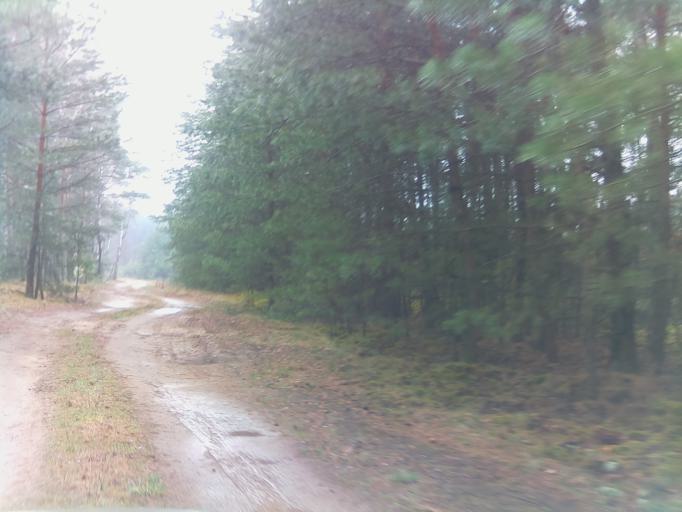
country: DE
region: Brandenburg
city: Jamlitz
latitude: 52.0514
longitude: 14.3600
